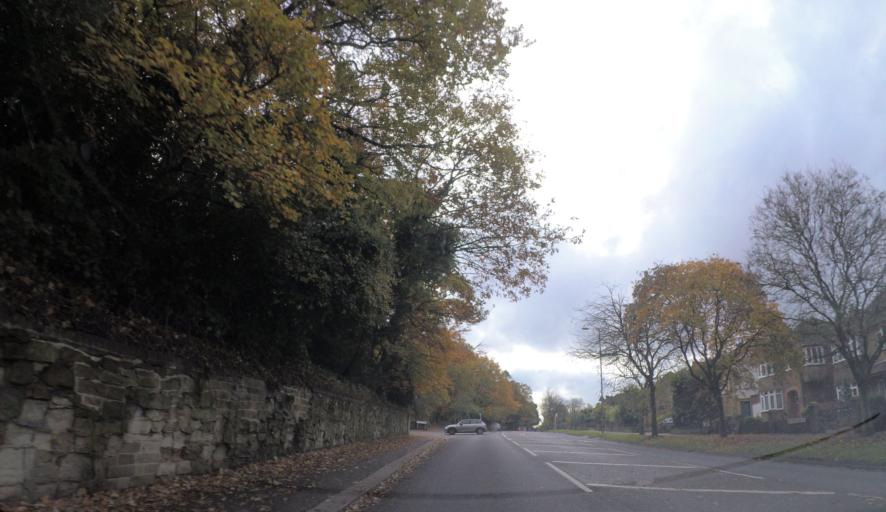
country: GB
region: England
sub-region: Surrey
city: Reigate
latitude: 51.2320
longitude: -0.2029
